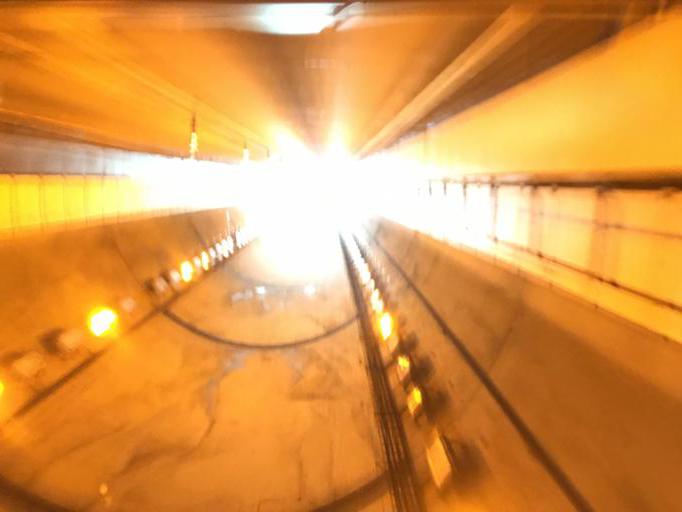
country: JP
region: Oita
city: Bungo-Takada-shi
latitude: 33.4840
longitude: 131.3317
